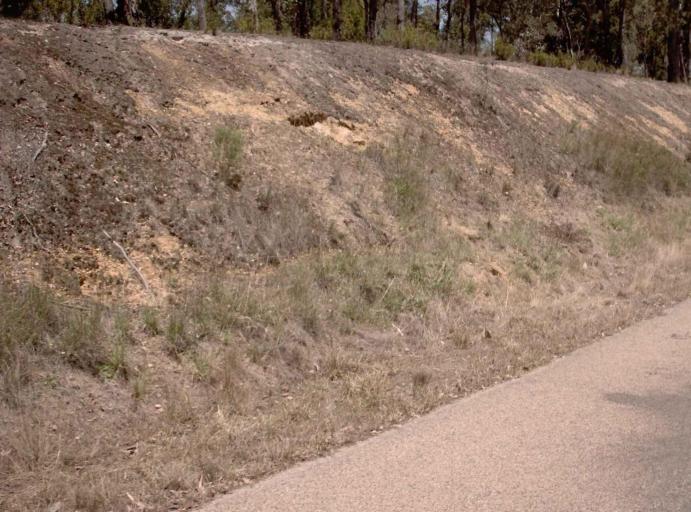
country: AU
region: Victoria
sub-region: East Gippsland
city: Bairnsdale
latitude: -37.7390
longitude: 147.7670
